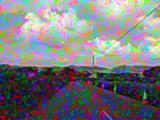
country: IE
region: Ulster
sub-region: County Donegal
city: Ramelton
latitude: 55.1989
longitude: -7.6387
